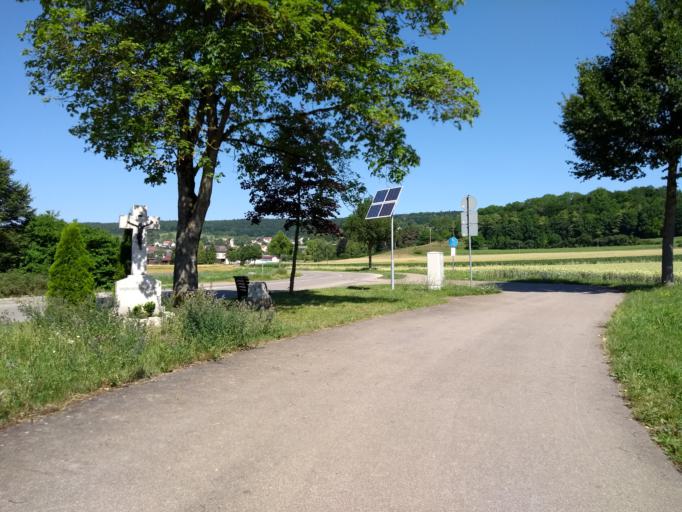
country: DE
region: Baden-Wuerttemberg
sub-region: Tuebingen Region
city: Munderkingen
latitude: 48.2690
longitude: 9.6413
